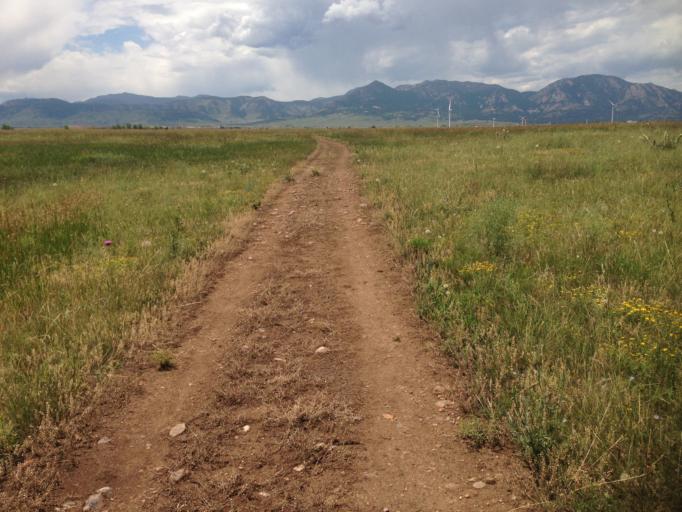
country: US
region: Colorado
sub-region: Boulder County
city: Superior
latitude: 39.9103
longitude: -105.1877
